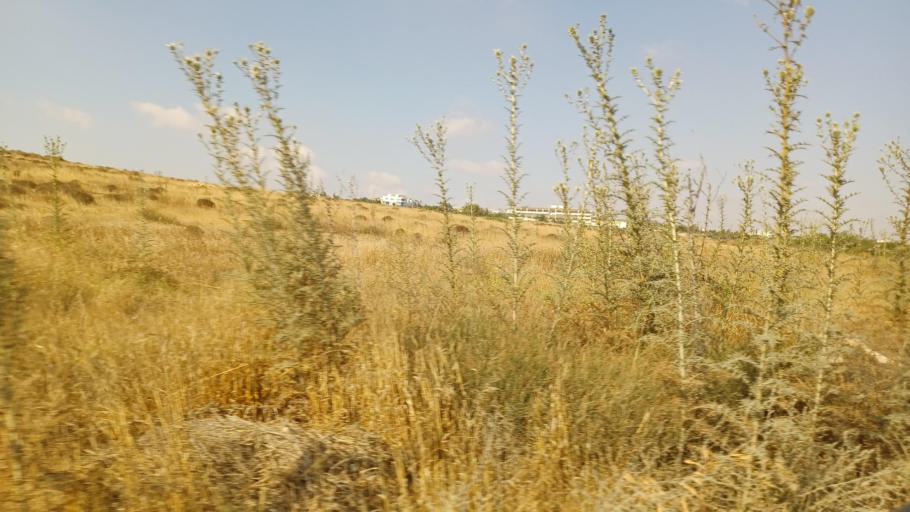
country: CY
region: Ammochostos
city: Deryneia
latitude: 35.0666
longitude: 33.9791
